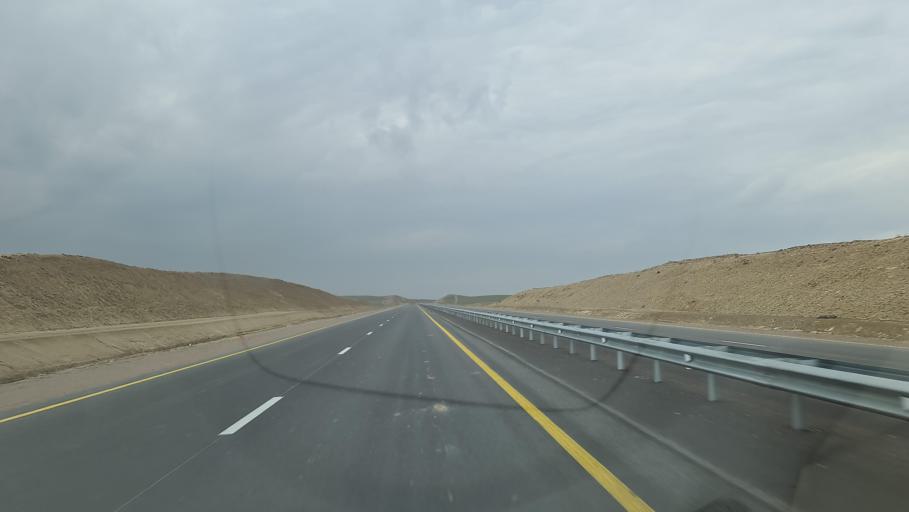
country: KG
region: Chuy
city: Bystrovka
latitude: 43.3205
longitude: 75.9056
